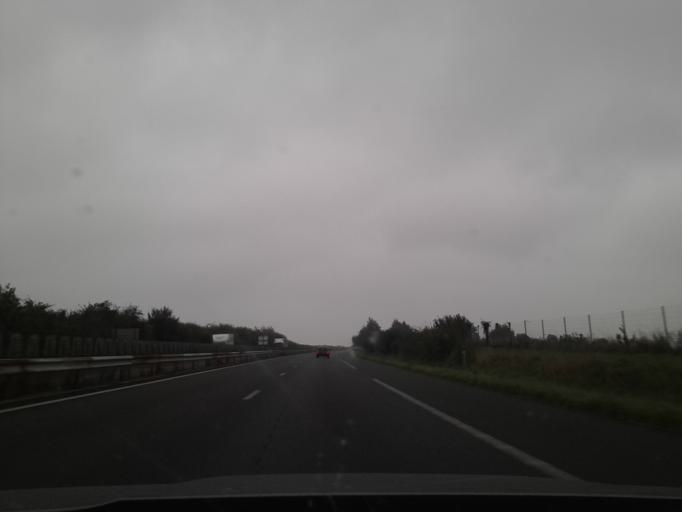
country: FR
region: Nord-Pas-de-Calais
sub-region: Departement du Nord
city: Fontaine-Notre-Dame
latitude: 50.1596
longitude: 3.1649
